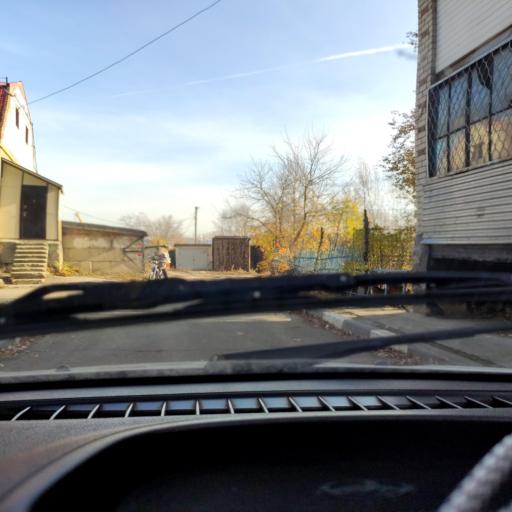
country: RU
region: Samara
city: Zhigulevsk
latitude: 53.4628
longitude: 49.5397
